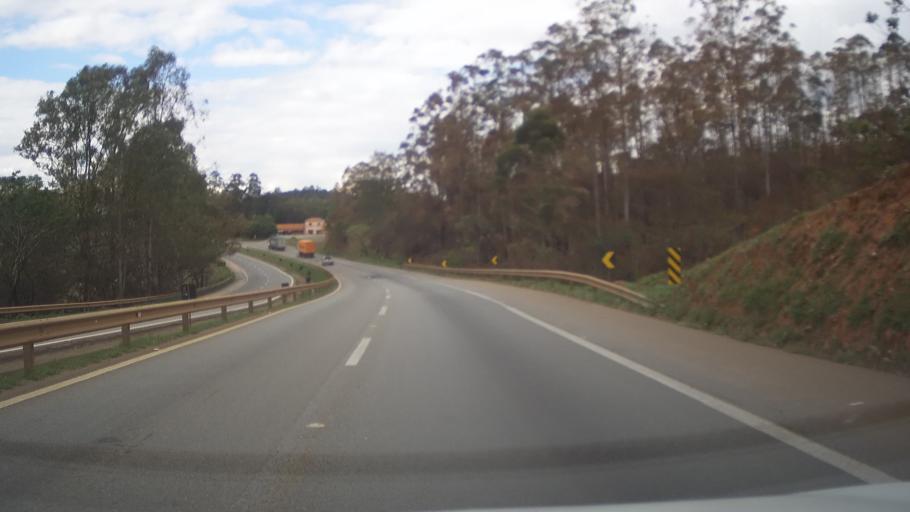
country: BR
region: Minas Gerais
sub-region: Itauna
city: Itauna
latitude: -20.2967
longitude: -44.4388
